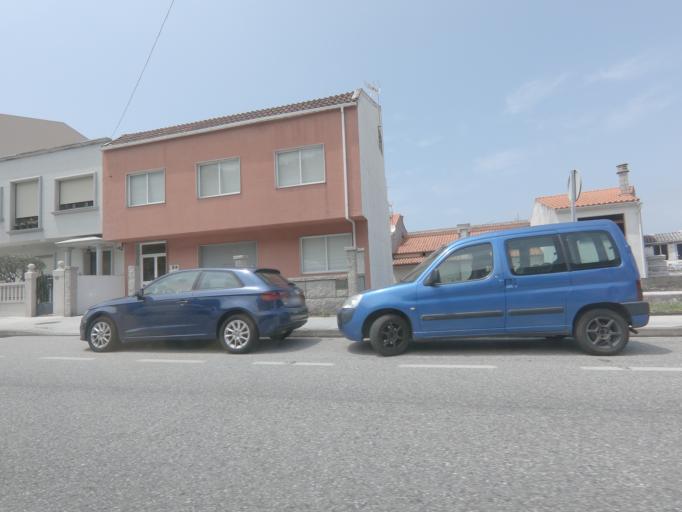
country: ES
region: Galicia
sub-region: Provincia de Pontevedra
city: A Guarda
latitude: 41.8977
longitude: -8.8737
